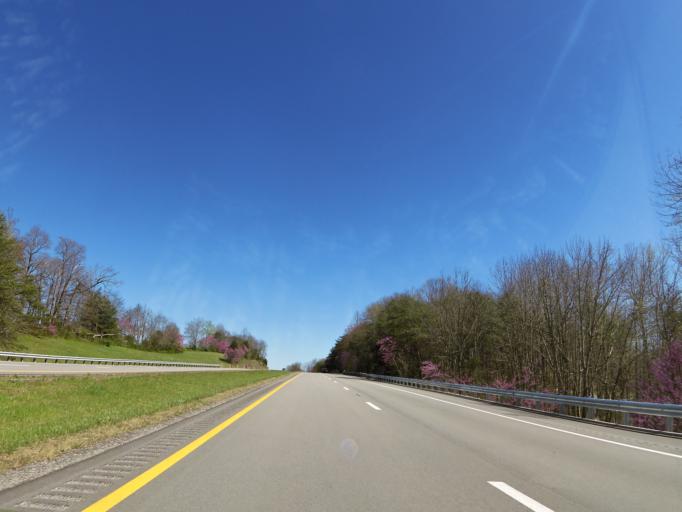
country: US
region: Kentucky
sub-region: Pulaski County
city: Somerset
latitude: 37.0944
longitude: -84.8228
